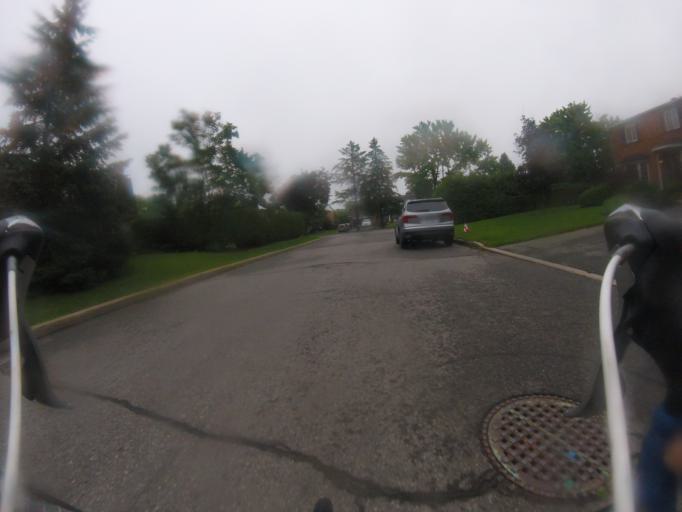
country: CA
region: Ontario
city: Bells Corners
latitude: 45.3365
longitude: -75.8014
